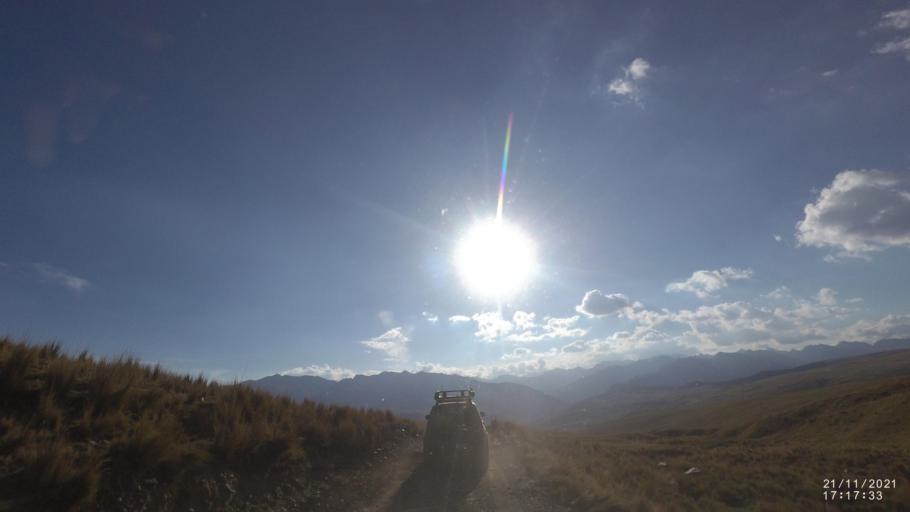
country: BO
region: Cochabamba
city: Cochabamba
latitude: -17.1431
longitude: -66.2564
